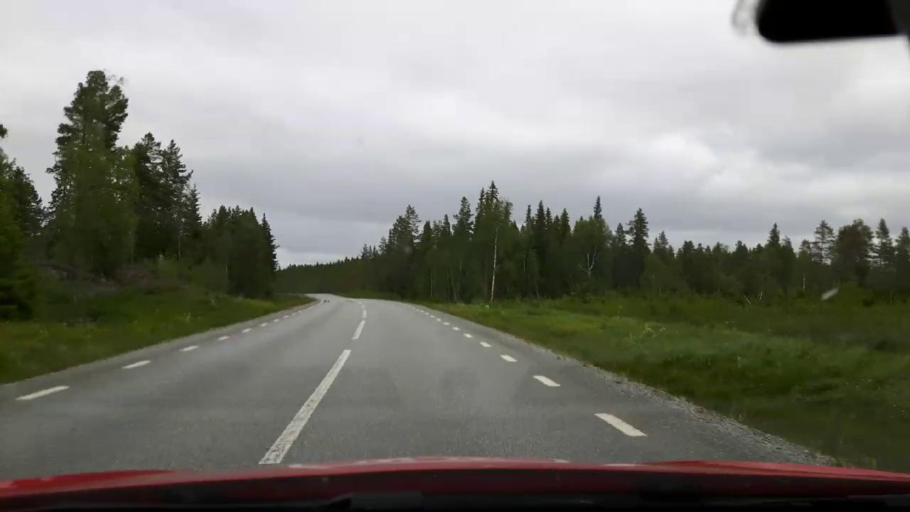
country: SE
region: Jaemtland
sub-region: OEstersunds Kommun
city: Lit
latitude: 63.6925
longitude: 14.6808
